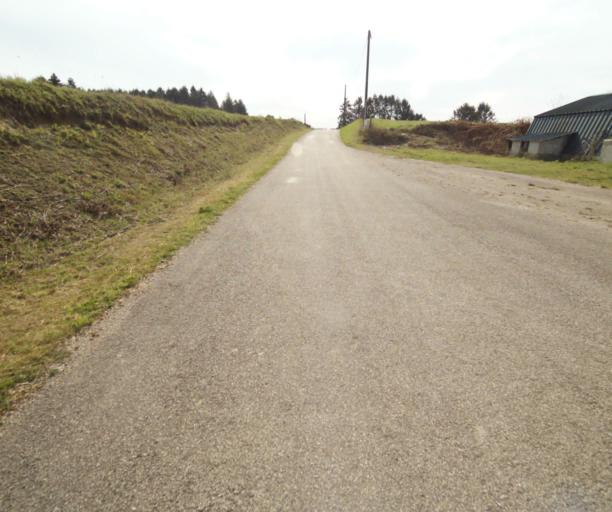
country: FR
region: Limousin
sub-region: Departement de la Correze
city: Correze
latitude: 45.3521
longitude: 1.8684
